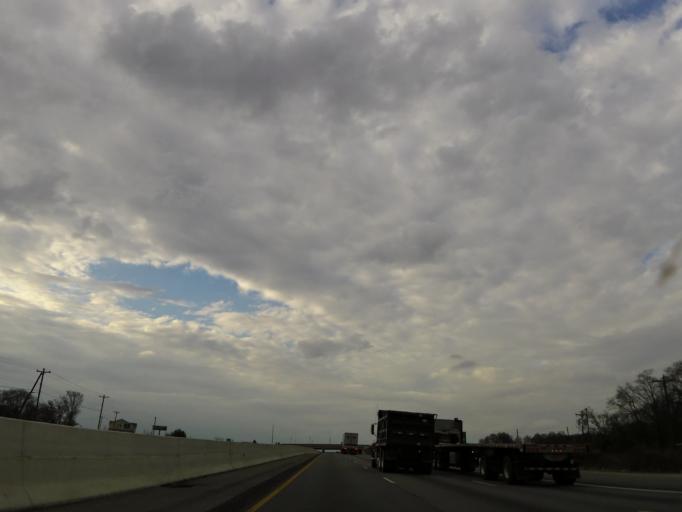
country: US
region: South Carolina
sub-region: Greenville County
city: Simpsonville
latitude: 34.7345
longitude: -82.2689
